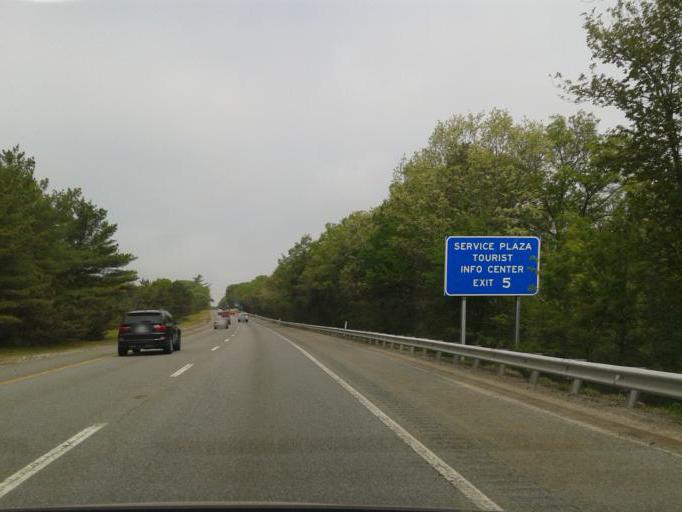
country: US
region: Massachusetts
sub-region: Plymouth County
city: Plymouth
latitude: 41.9205
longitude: -70.6244
